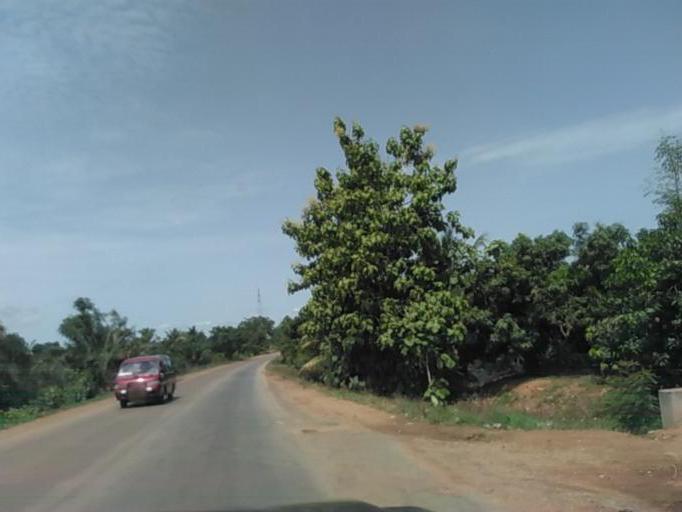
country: GH
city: Akropong
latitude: 6.1715
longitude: 0.0689
